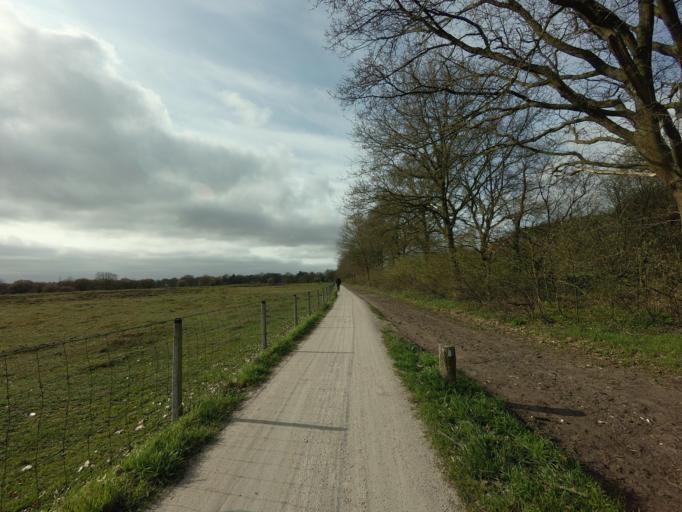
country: NL
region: North Holland
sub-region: Gemeente Blaricum
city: Blaricum
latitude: 52.2820
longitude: 5.2517
